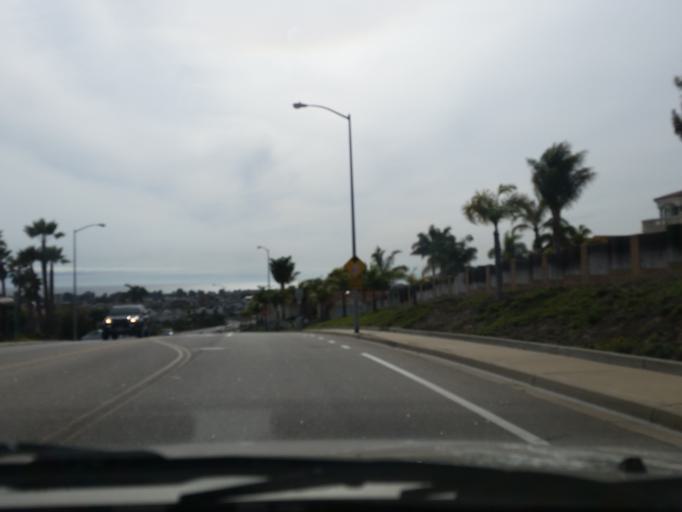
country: US
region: California
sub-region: San Luis Obispo County
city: Grover Beach
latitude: 35.1375
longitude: -120.6206
